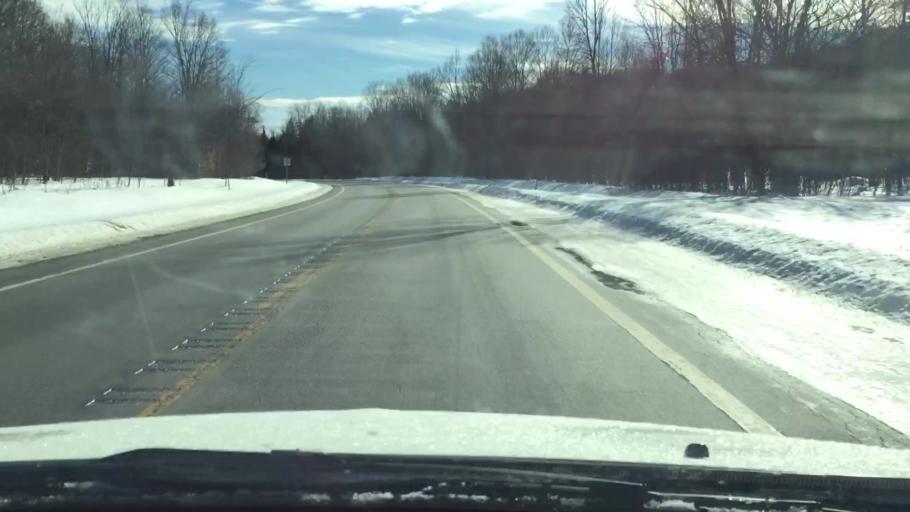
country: US
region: Michigan
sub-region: Antrim County
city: Mancelona
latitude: 45.0093
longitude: -85.0648
